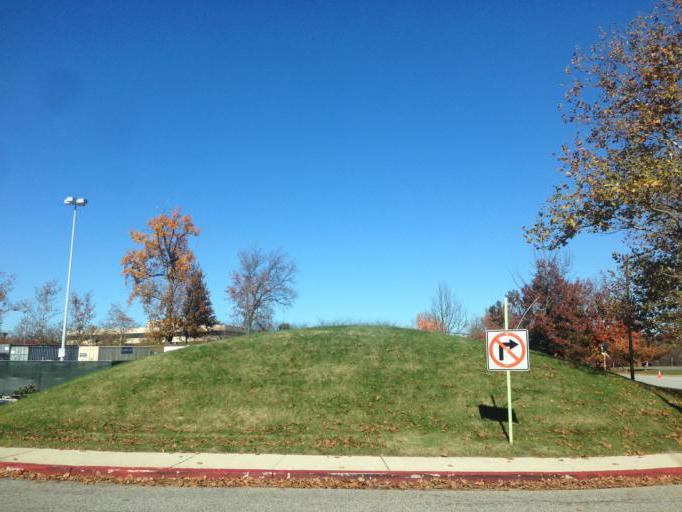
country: US
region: Maryland
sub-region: Howard County
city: Columbia
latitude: 39.2175
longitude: -76.8585
